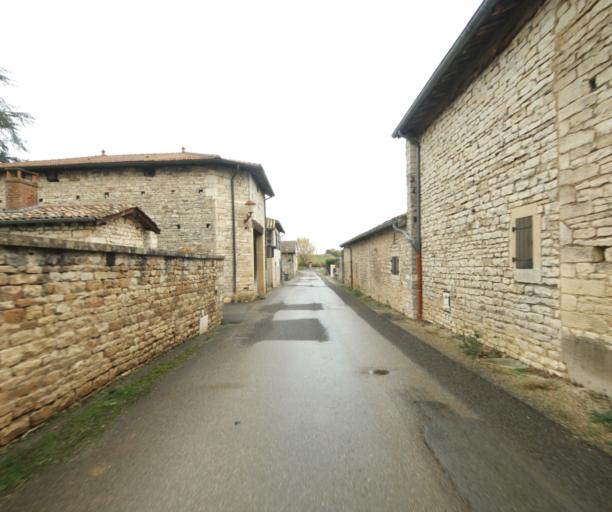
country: FR
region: Rhone-Alpes
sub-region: Departement de l'Ain
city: Pont-de-Vaux
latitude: 46.4737
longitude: 4.8933
